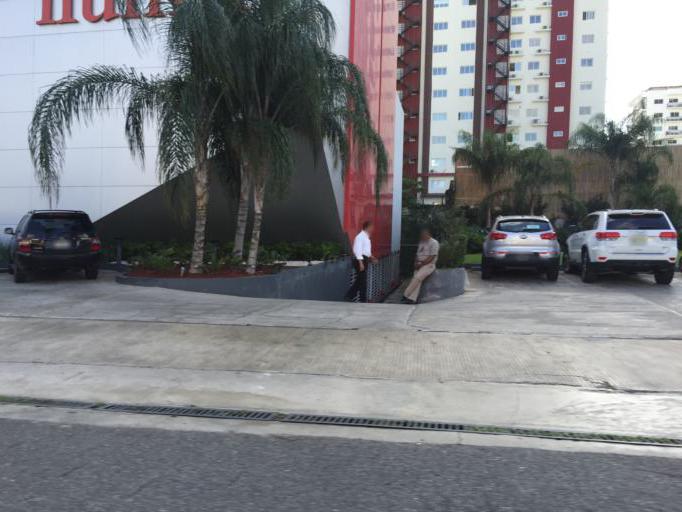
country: DO
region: Nacional
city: La Julia
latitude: 18.4784
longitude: -69.9375
